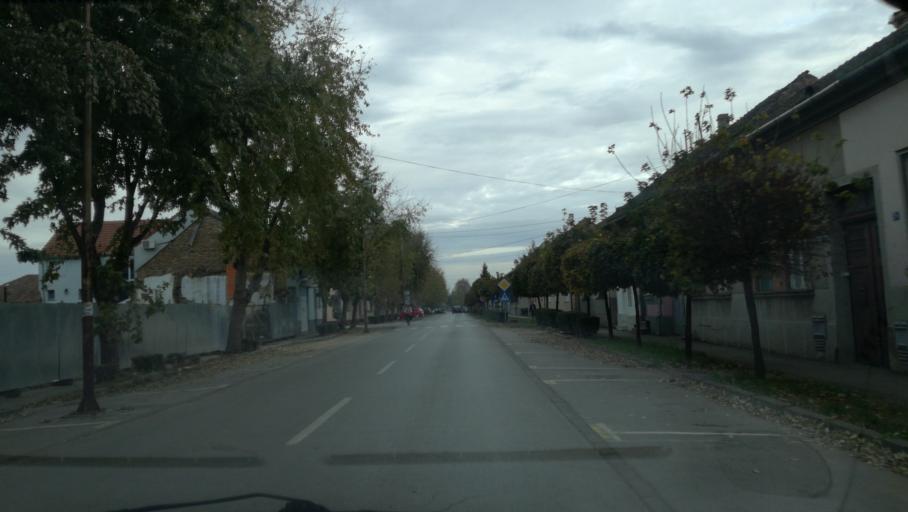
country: RS
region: Autonomna Pokrajina Vojvodina
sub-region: Severnobanatski Okrug
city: Kikinda
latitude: 45.8338
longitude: 20.4670
